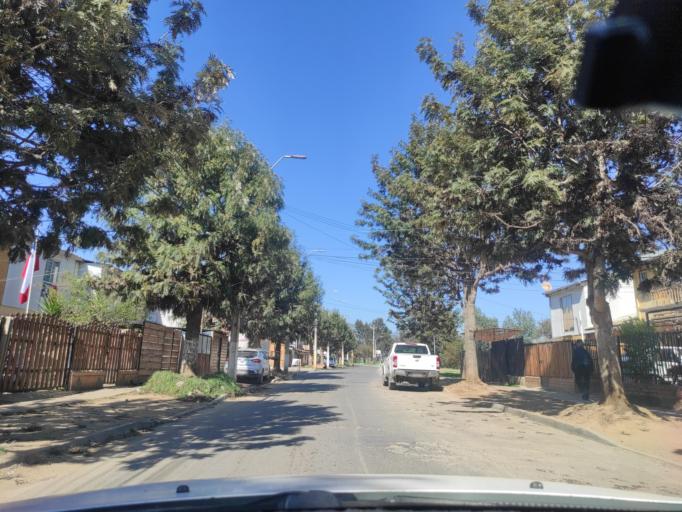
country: CL
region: Valparaiso
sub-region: Provincia de Marga Marga
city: Limache
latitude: -33.0185
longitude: -71.2639
